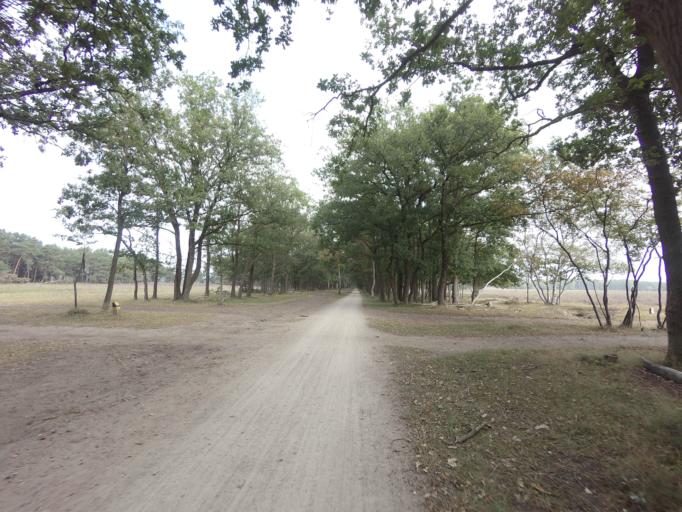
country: NL
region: North Holland
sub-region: Gemeente Bussum
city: Bussum
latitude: 52.2558
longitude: 5.1868
